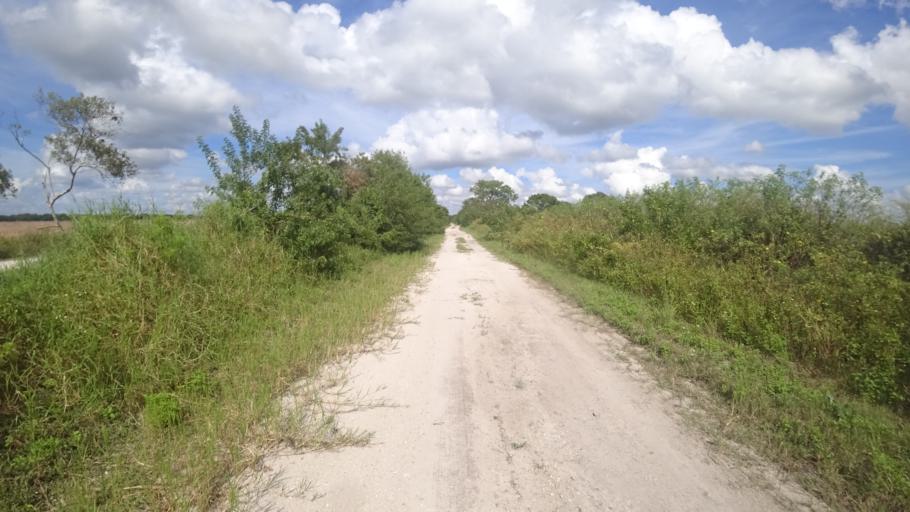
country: US
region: Florida
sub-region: Hillsborough County
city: Wimauma
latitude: 27.5878
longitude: -82.2665
